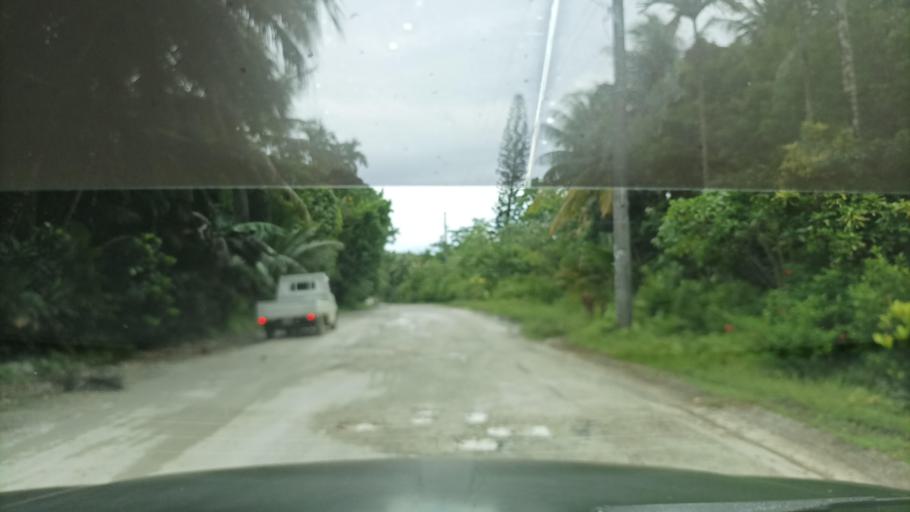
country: FM
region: Yap
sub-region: Weloy Municipality
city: Colonia
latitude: 9.5466
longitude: 138.1492
